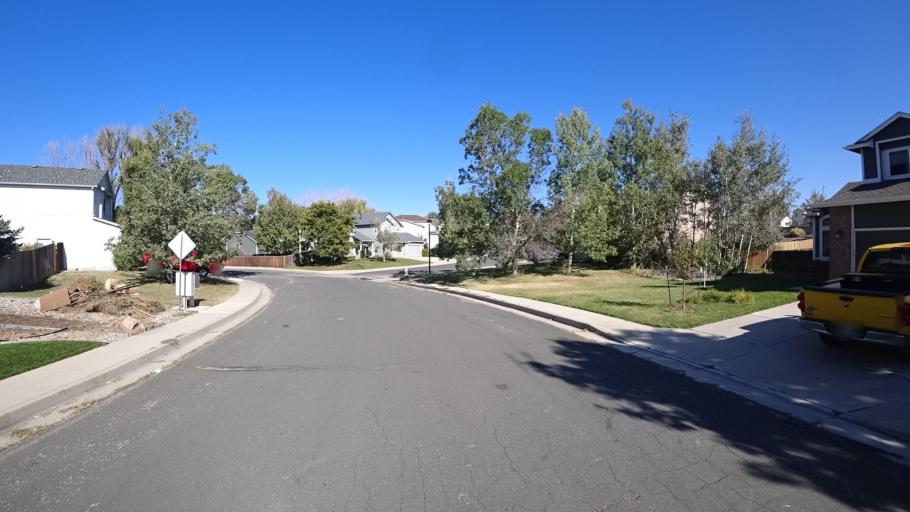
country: US
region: Colorado
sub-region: El Paso County
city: Cimarron Hills
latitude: 38.8795
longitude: -104.7021
